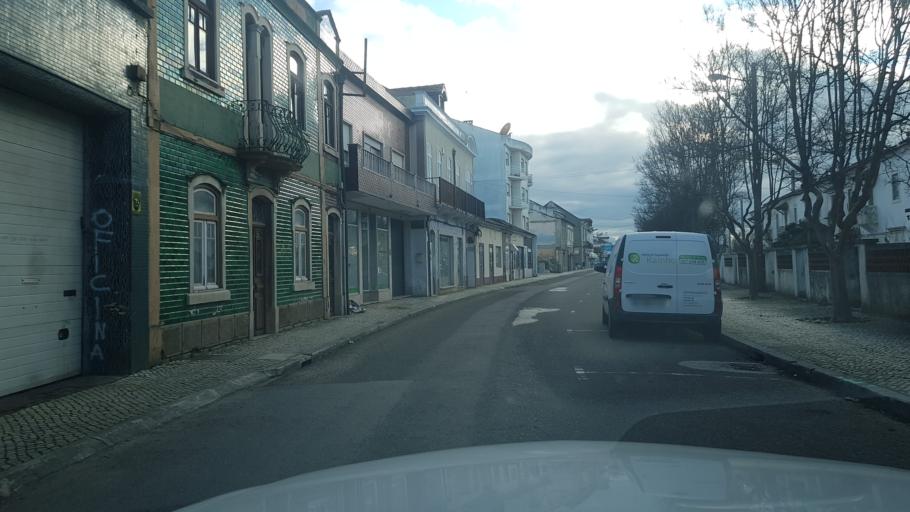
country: PT
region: Santarem
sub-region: Entroncamento
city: Entroncamento
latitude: 39.4626
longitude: -8.4717
